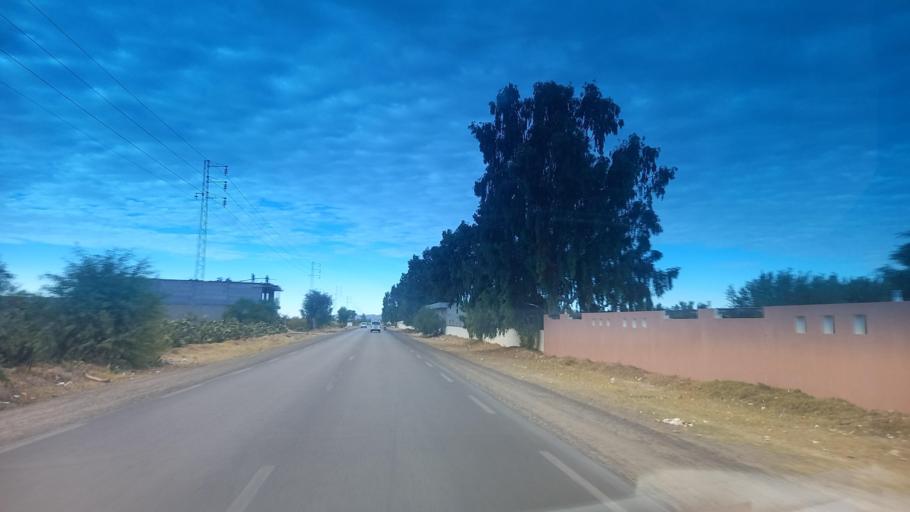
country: TN
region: Al Qasrayn
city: Kasserine
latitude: 35.2673
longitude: 9.0931
